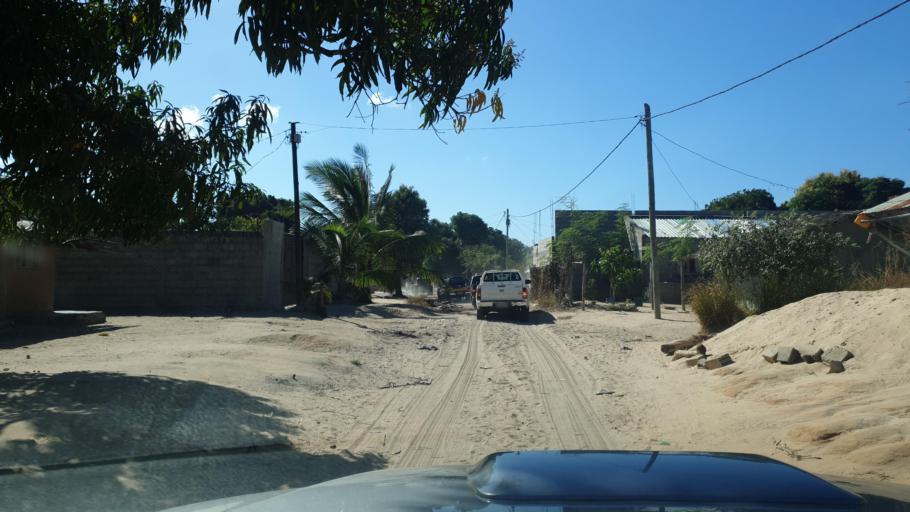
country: MZ
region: Nampula
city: Nacala
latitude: -14.5353
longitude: 40.7043
